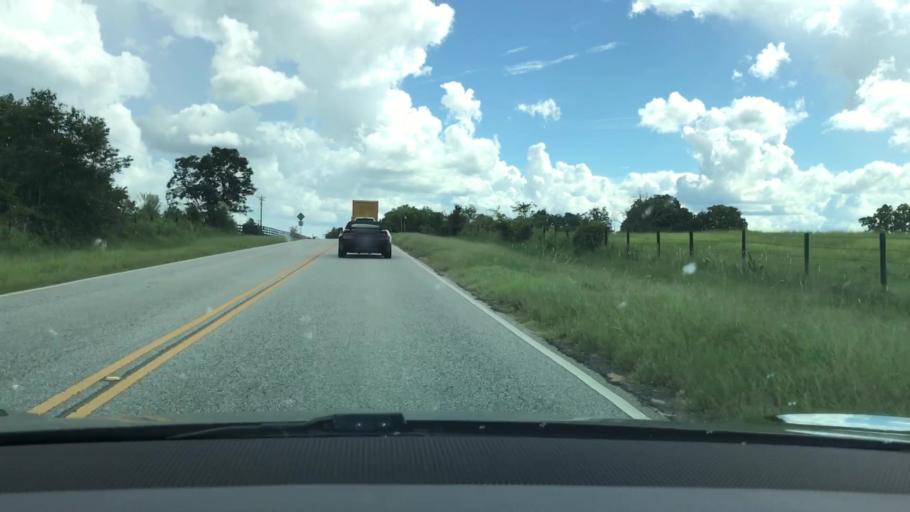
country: US
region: Alabama
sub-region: Montgomery County
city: Pike Road
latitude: 32.2521
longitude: -86.0934
